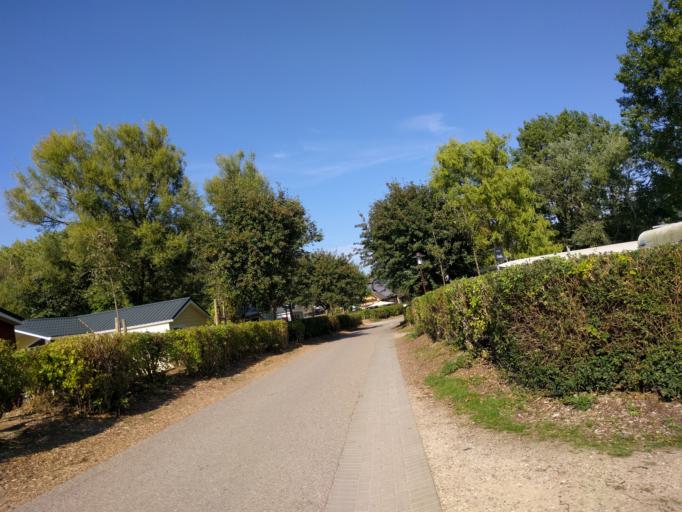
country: DE
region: Schleswig-Holstein
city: Burg auf Fehmarn
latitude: 54.4047
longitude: 11.1763
